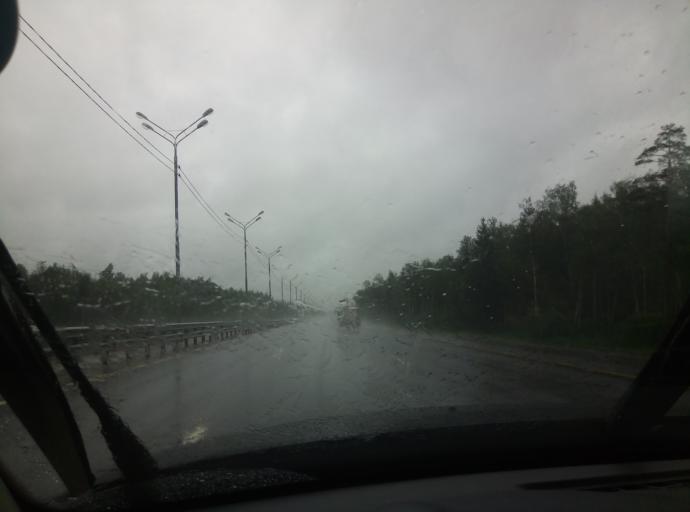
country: RU
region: Moskovskaya
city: Danki
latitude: 54.9919
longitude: 37.5392
